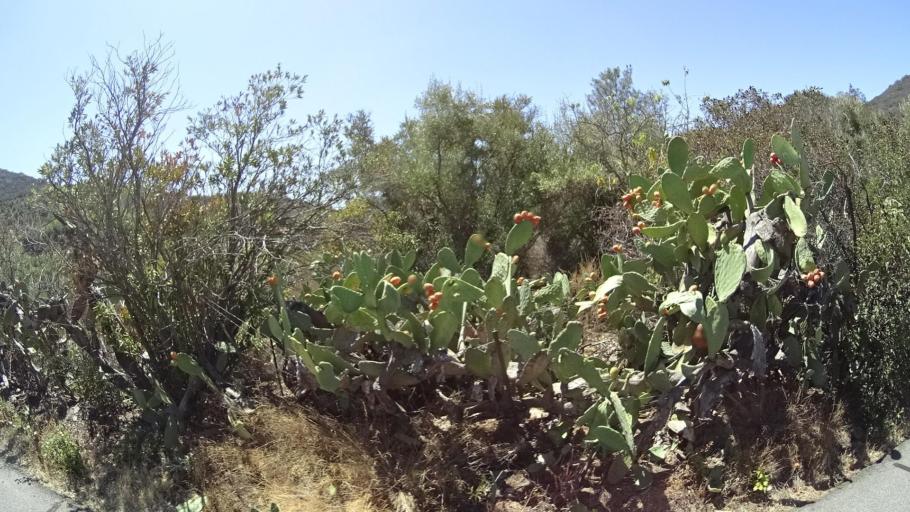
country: US
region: California
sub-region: San Diego County
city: Rainbow
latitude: 33.3915
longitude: -117.1091
